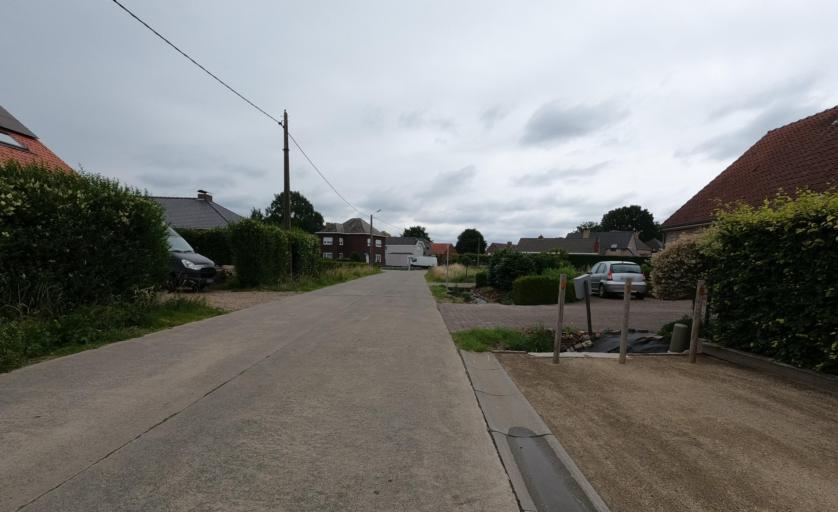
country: BE
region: Flanders
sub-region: Provincie Antwerpen
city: Berlaar
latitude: 51.0940
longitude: 4.6746
